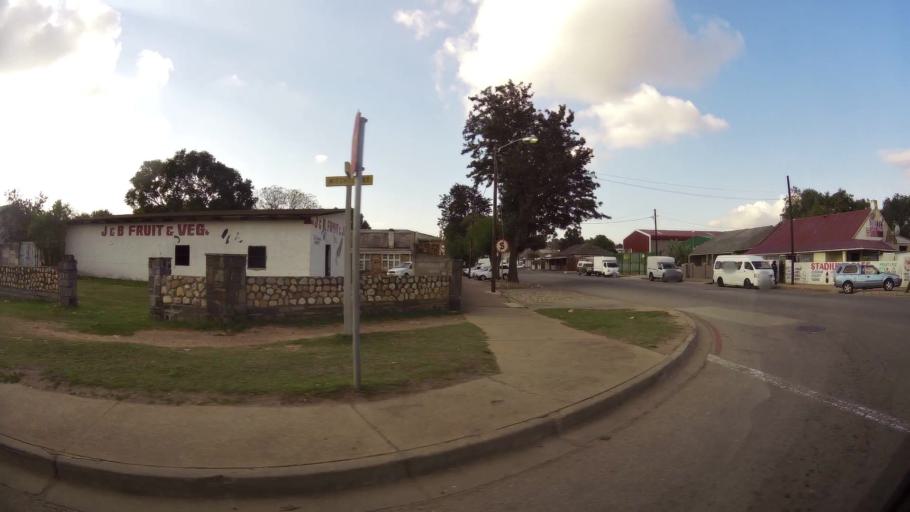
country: ZA
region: Eastern Cape
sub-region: Nelson Mandela Bay Metropolitan Municipality
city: Uitenhage
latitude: -33.7732
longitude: 25.3959
